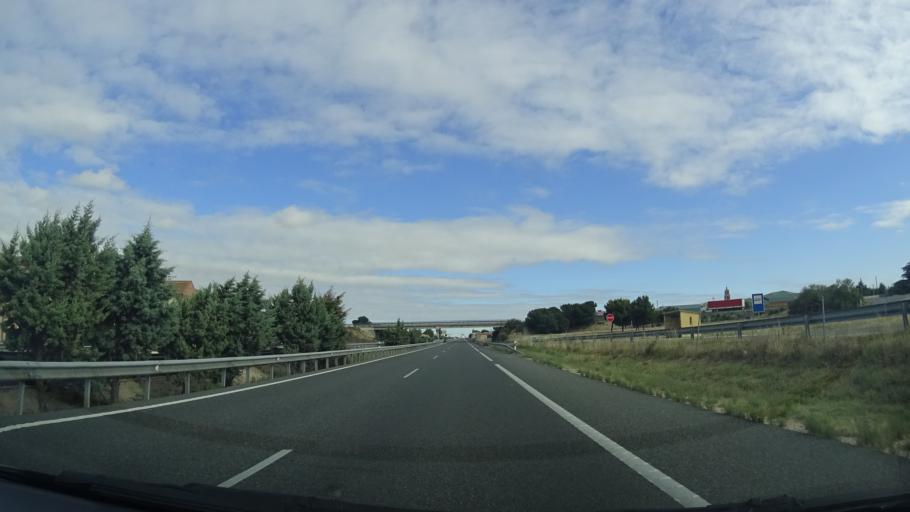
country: ES
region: Castille and Leon
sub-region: Provincia de Valladolid
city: Ataquines
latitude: 41.1757
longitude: -4.8046
